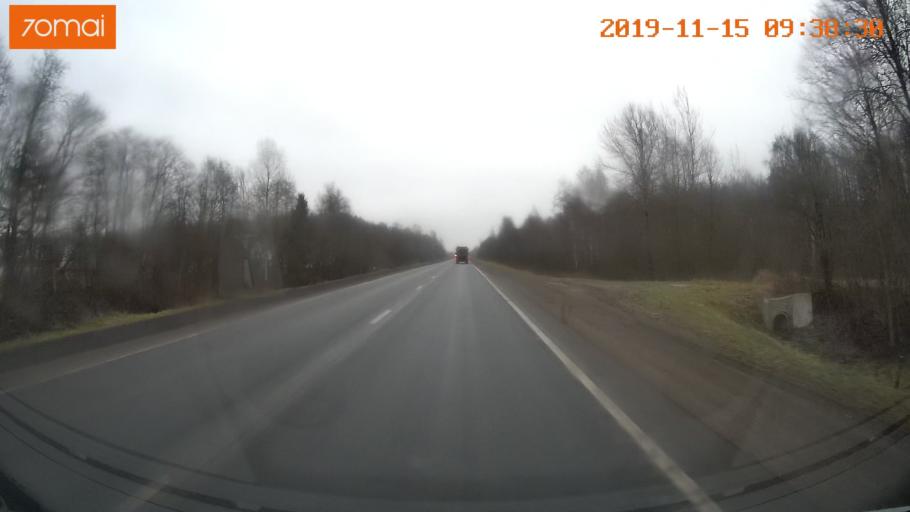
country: RU
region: Vologda
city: Sheksna
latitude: 59.2314
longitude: 38.4567
